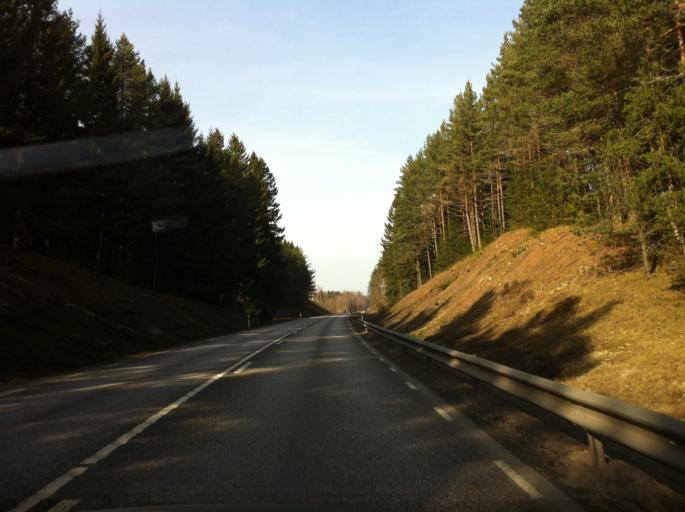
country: SE
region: Vaestra Goetaland
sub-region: Skovde Kommun
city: Skultorp
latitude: 58.2456
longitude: 13.8174
